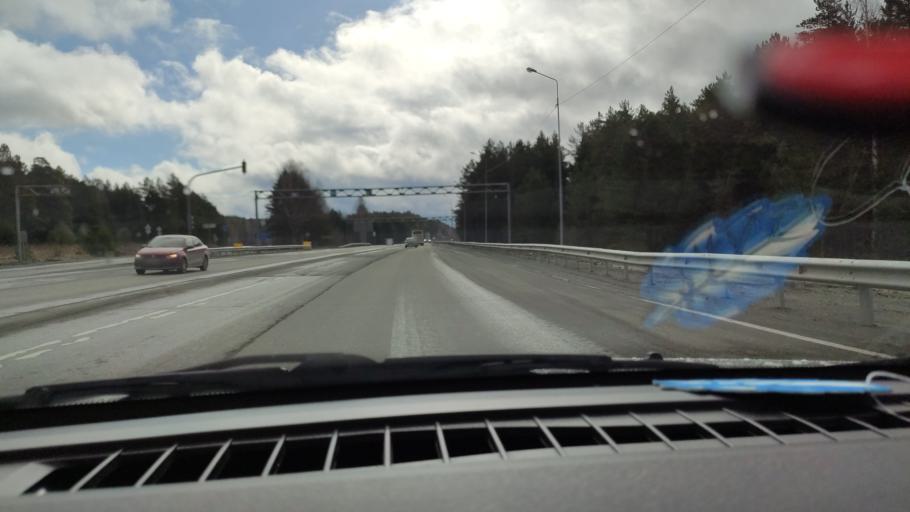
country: RU
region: Sverdlovsk
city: Talitsa
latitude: 56.8729
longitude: 60.0360
